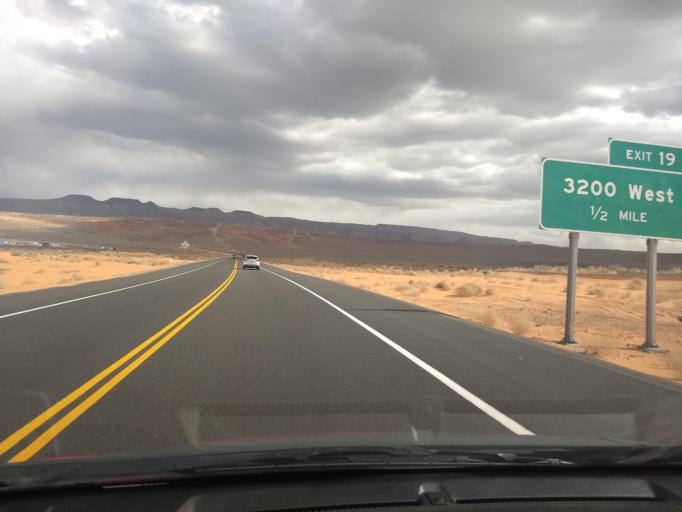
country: US
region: Utah
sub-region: Washington County
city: Hurricane
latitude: 37.0989
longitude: -113.3746
